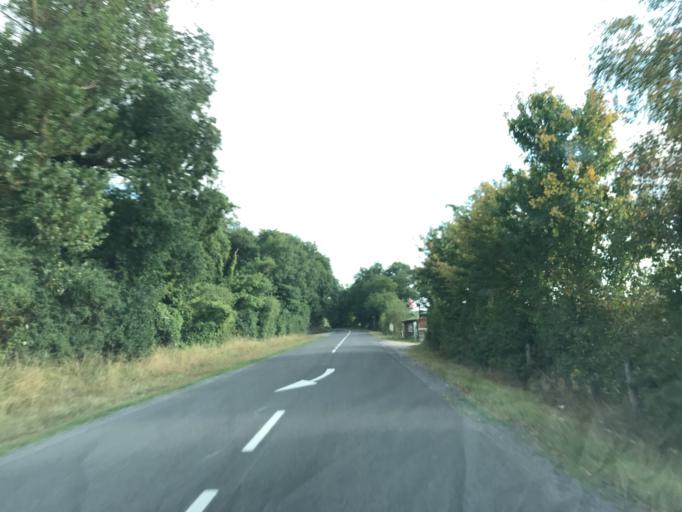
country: FR
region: Haute-Normandie
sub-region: Departement de l'Eure
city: Courcelles-sur-Seine
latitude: 49.1986
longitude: 1.3839
